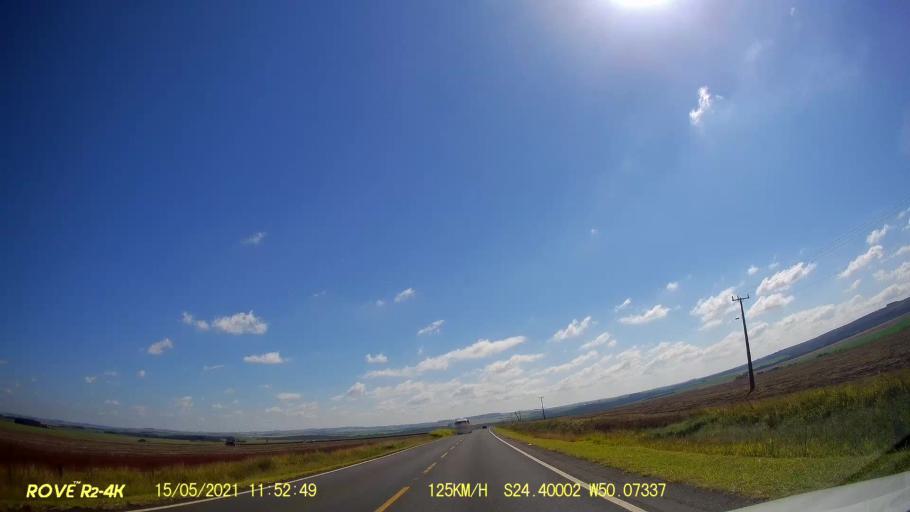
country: BR
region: Parana
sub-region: Pirai Do Sul
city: Pirai do Sul
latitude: -24.4004
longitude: -50.0735
